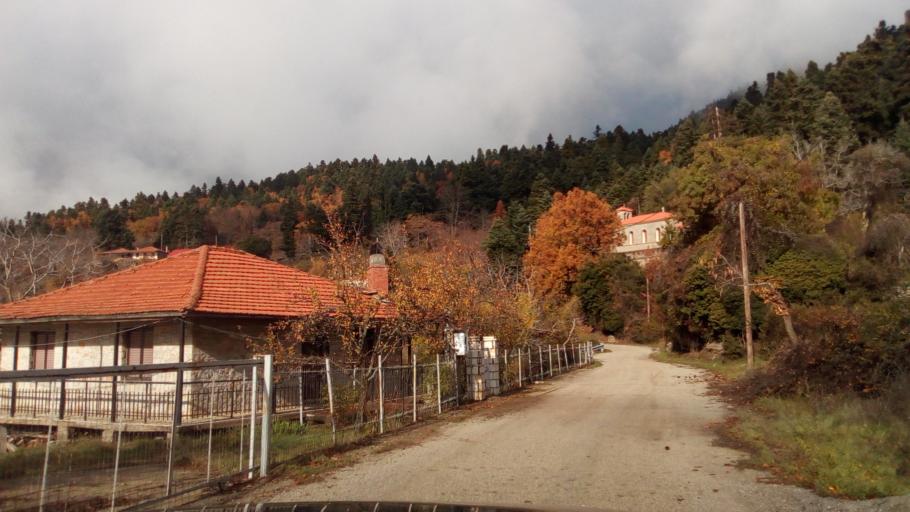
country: GR
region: West Greece
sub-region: Nomos Aitolias kai Akarnanias
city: Nafpaktos
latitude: 38.5671
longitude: 21.9209
